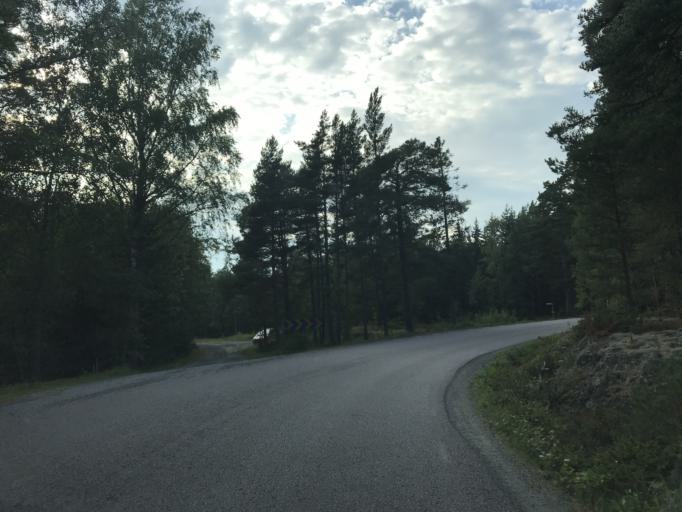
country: SE
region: Stockholm
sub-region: Norrtalje Kommun
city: Bjorko
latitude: 59.8783
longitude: 18.9852
